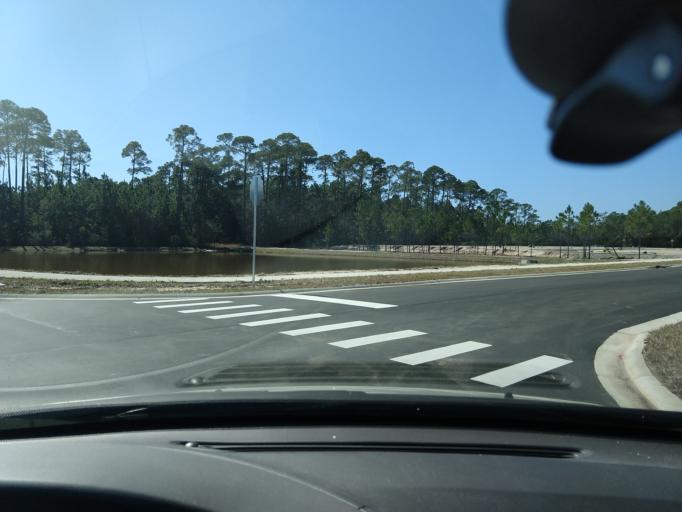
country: US
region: Florida
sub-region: Walton County
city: Miramar Beach
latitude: 30.3827
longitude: -86.2898
